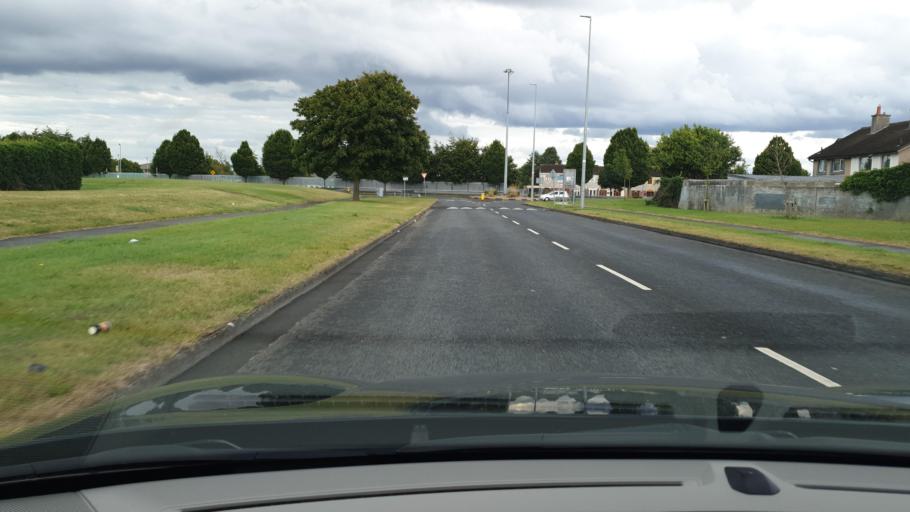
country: IE
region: Leinster
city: Clondalkin
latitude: 53.3407
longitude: -6.4012
